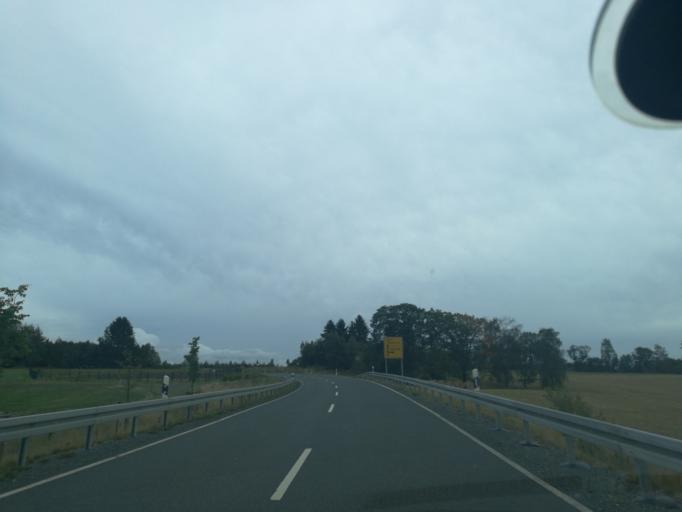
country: DE
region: Bavaria
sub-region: Upper Franconia
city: Regnitzlosau
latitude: 50.3363
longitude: 12.0795
